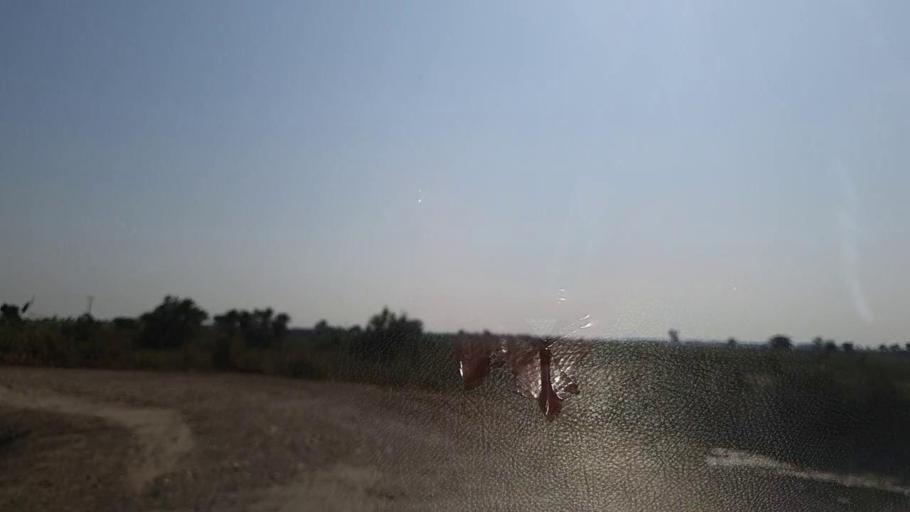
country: PK
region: Sindh
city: Sanghar
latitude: 25.9895
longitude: 69.0605
